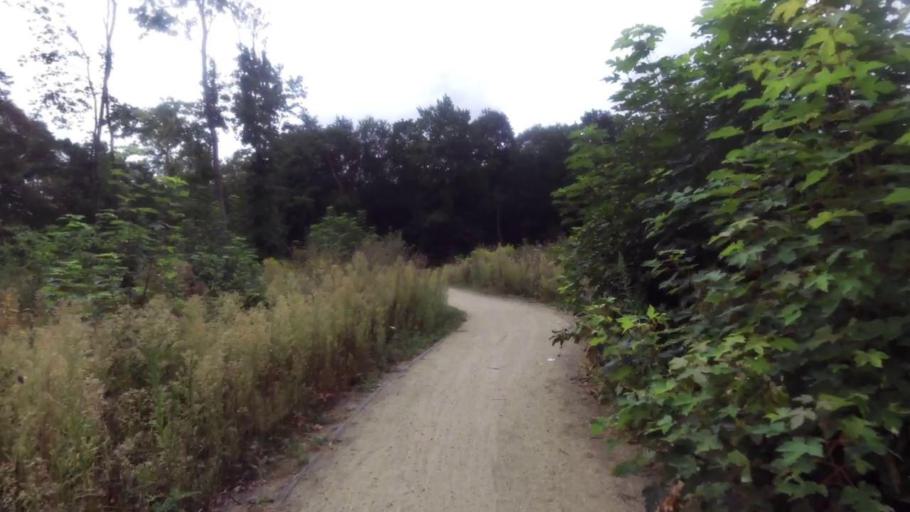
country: PL
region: West Pomeranian Voivodeship
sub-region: Powiat mysliborski
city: Debno
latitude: 52.7176
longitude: 14.6930
